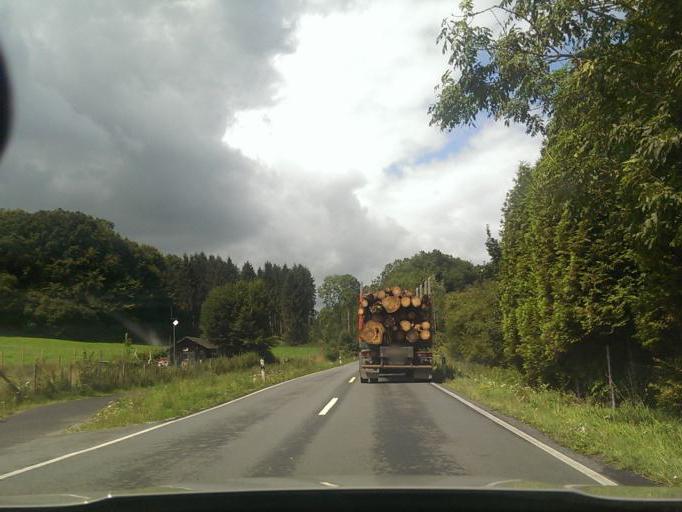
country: DE
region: North Rhine-Westphalia
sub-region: Regierungsbezirk Detmold
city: Hoexter
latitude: 51.8221
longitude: 9.3776
